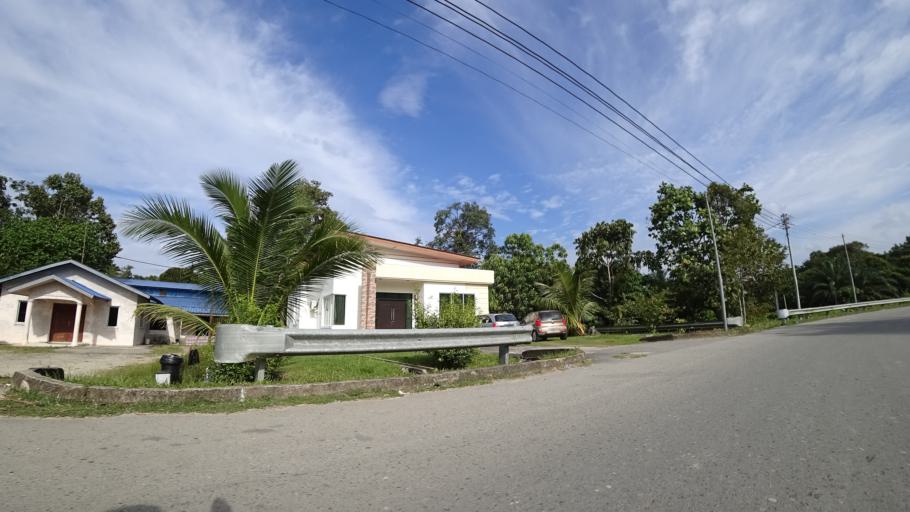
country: BN
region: Brunei and Muara
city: Bandar Seri Begawan
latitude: 4.8727
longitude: 114.8077
